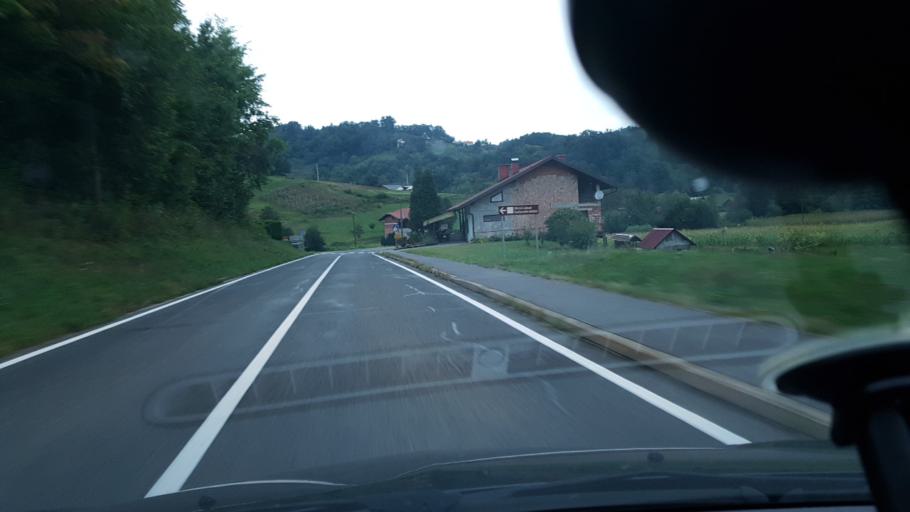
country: HR
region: Krapinsko-Zagorska
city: Pregrada
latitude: 46.2084
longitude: 15.7502
